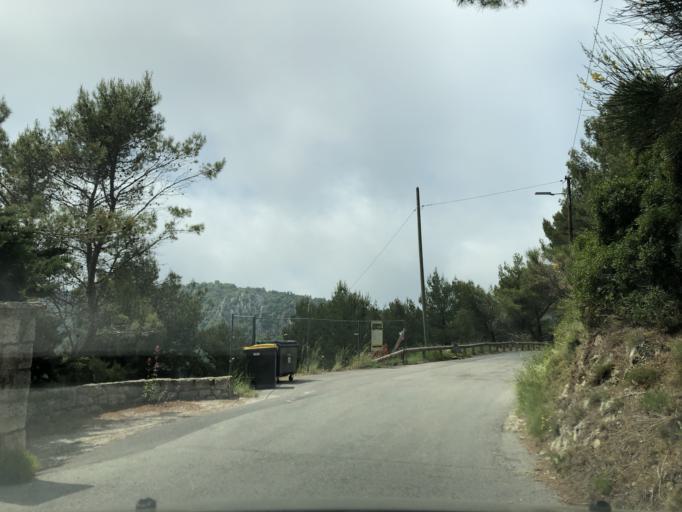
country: FR
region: Provence-Alpes-Cote d'Azur
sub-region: Departement des Alpes-Maritimes
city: Eze
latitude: 43.7360
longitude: 7.3495
